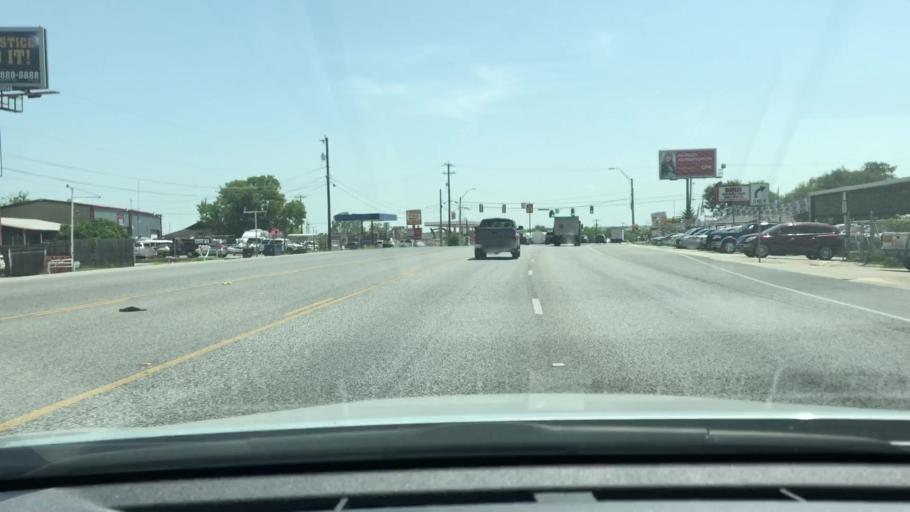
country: US
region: Texas
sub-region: Bexar County
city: Kirby
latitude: 29.4740
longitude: -98.3825
